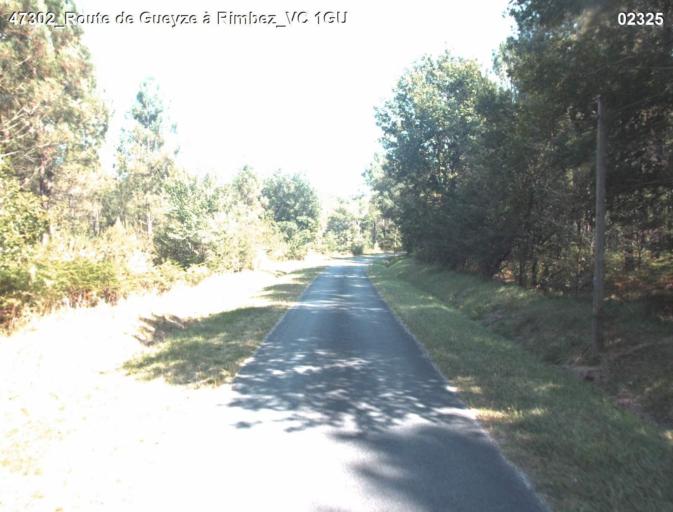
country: FR
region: Aquitaine
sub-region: Departement des Landes
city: Gabarret
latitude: 44.0426
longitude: 0.1084
